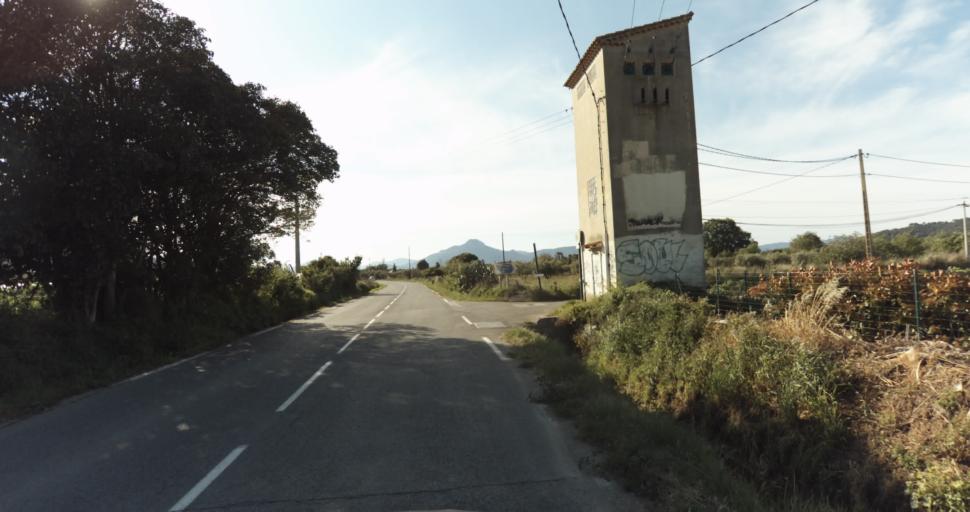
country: FR
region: Provence-Alpes-Cote d'Azur
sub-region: Departement du Var
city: Carqueiranne
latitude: 43.1164
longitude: 6.0907
